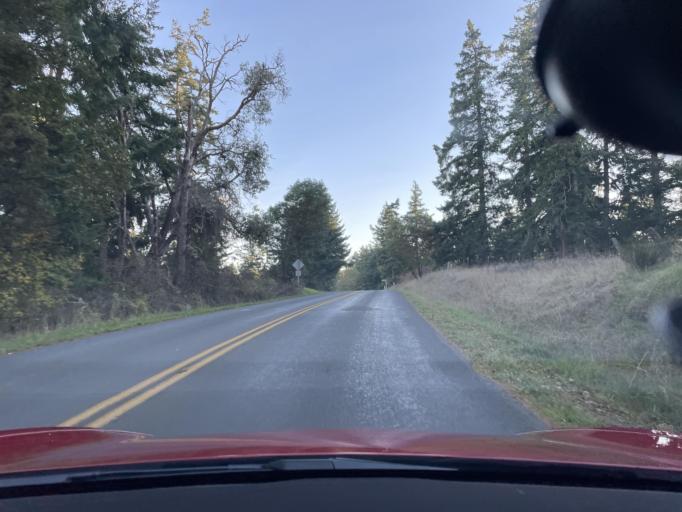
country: US
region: Washington
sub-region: San Juan County
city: Friday Harbor
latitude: 48.5646
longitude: -123.1538
